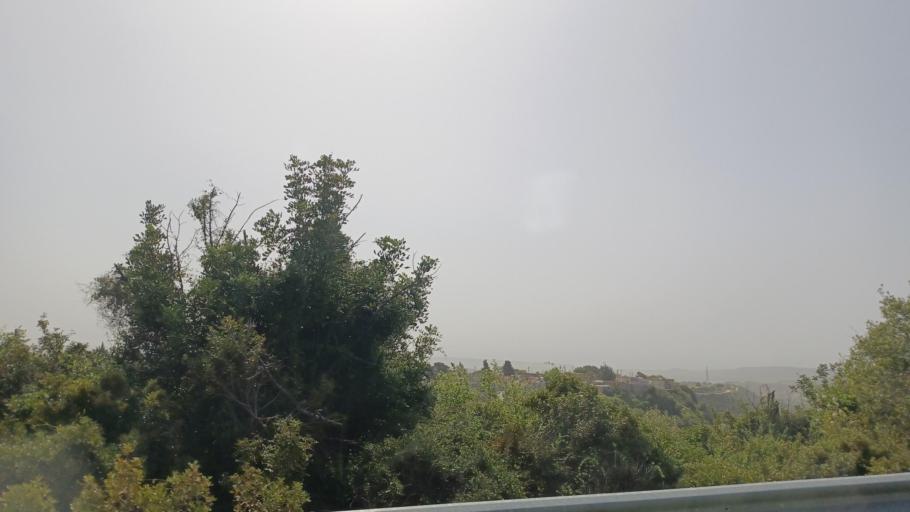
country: CY
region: Limassol
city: Pissouri
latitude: 34.7181
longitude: 32.7224
